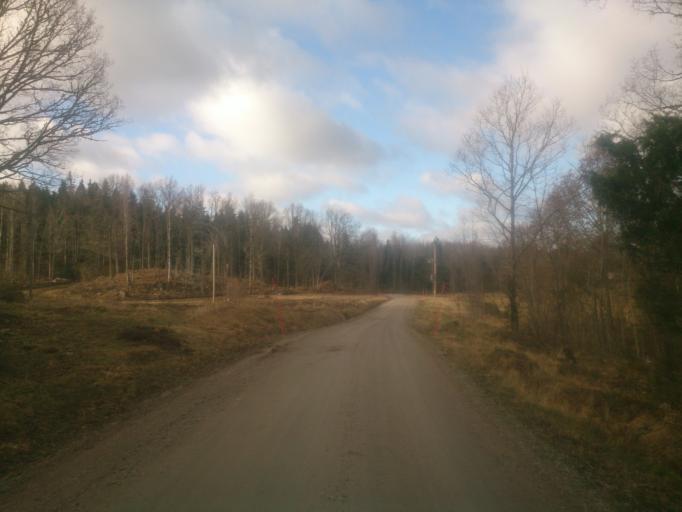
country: SE
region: OEstergoetland
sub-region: Atvidabergs Kommun
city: Atvidaberg
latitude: 58.2047
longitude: 16.1593
